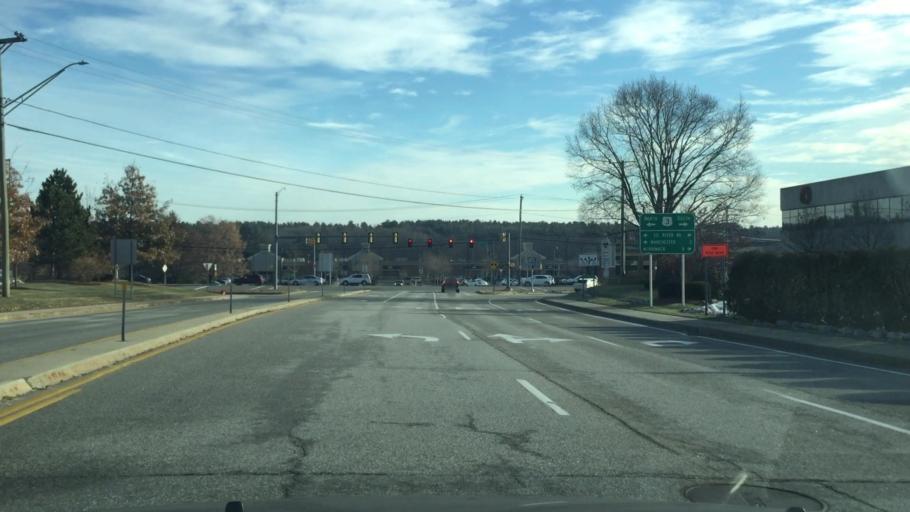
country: US
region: New Hampshire
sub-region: Hillsborough County
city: Bedford
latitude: 42.9568
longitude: -71.4801
